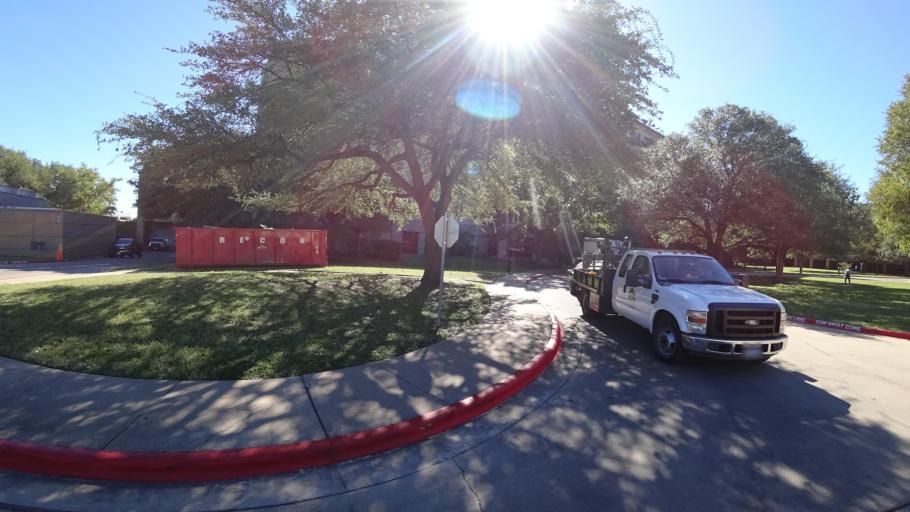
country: US
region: Texas
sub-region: Travis County
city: Austin
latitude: 30.3182
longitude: -97.7321
